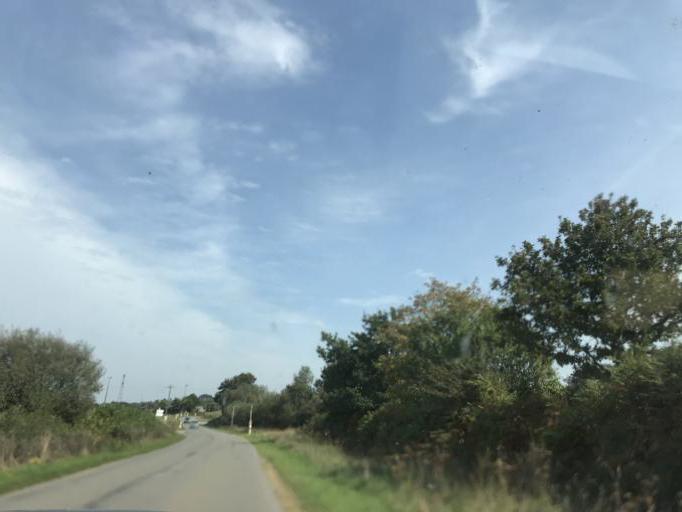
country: FR
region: Brittany
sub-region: Departement du Finistere
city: Hanvec
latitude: 48.2881
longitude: -4.1123
